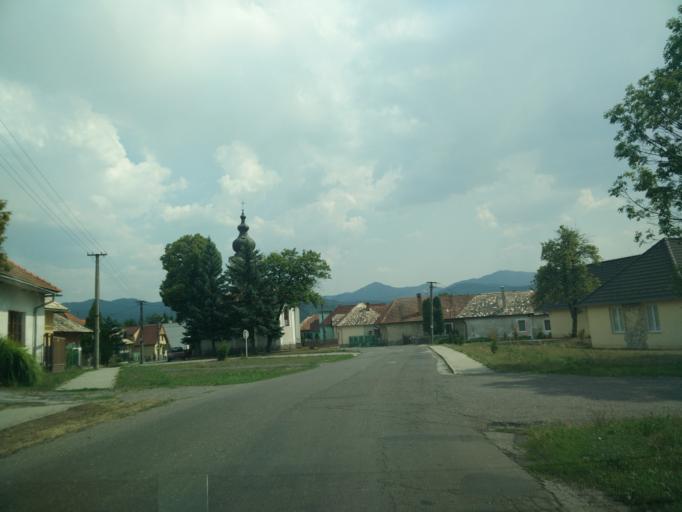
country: SK
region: Banskobystricky
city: Zarnovica
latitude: 48.5452
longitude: 18.7628
